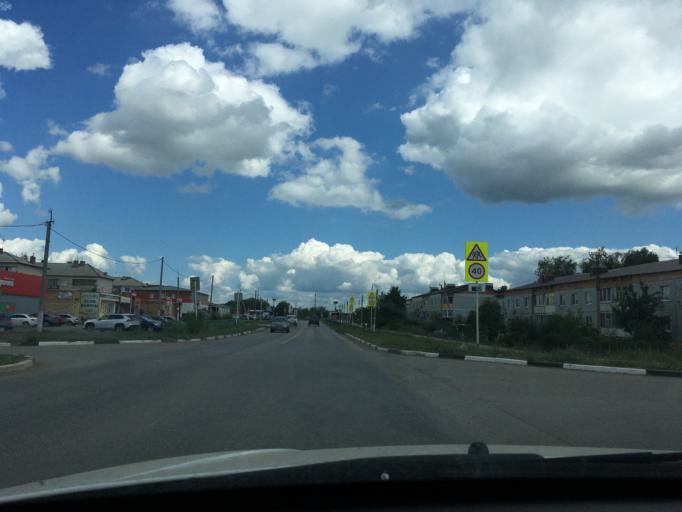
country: RU
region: Samara
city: Bezenchuk
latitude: 52.9930
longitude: 49.4374
